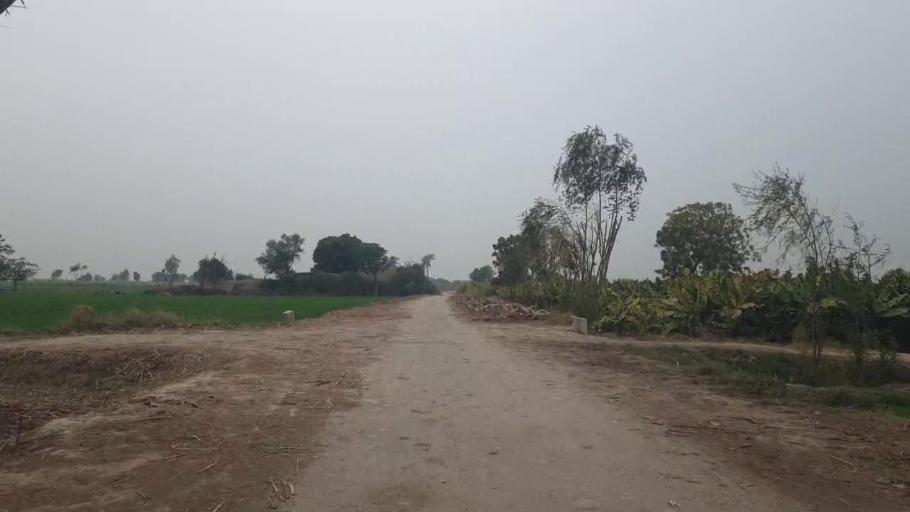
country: PK
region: Sindh
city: Shahdadpur
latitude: 25.8650
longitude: 68.6166
